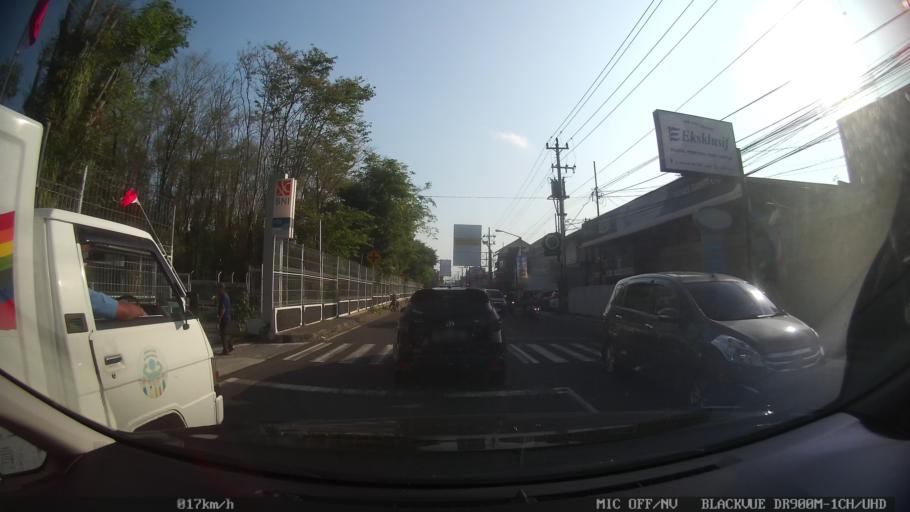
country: ID
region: Daerah Istimewa Yogyakarta
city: Depok
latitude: -7.7631
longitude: 110.4118
